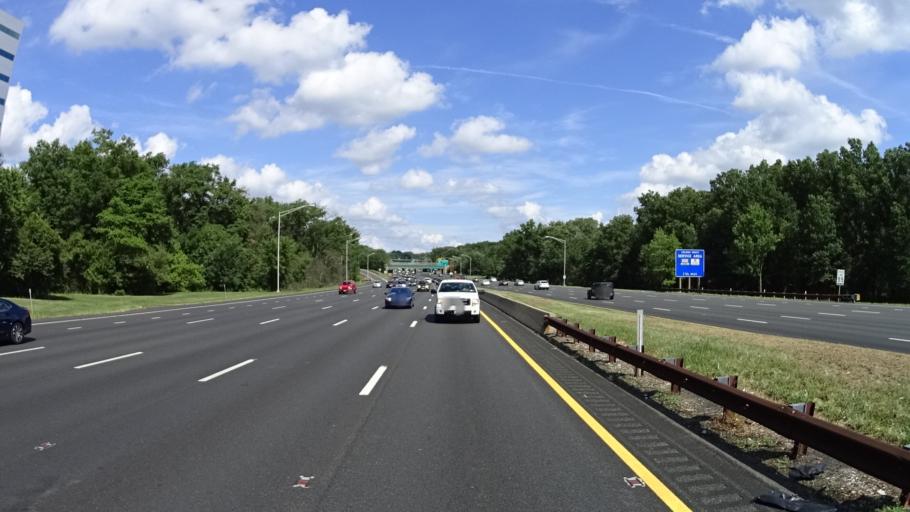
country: US
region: New Jersey
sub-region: Middlesex County
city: Iselin
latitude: 40.5653
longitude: -74.3244
